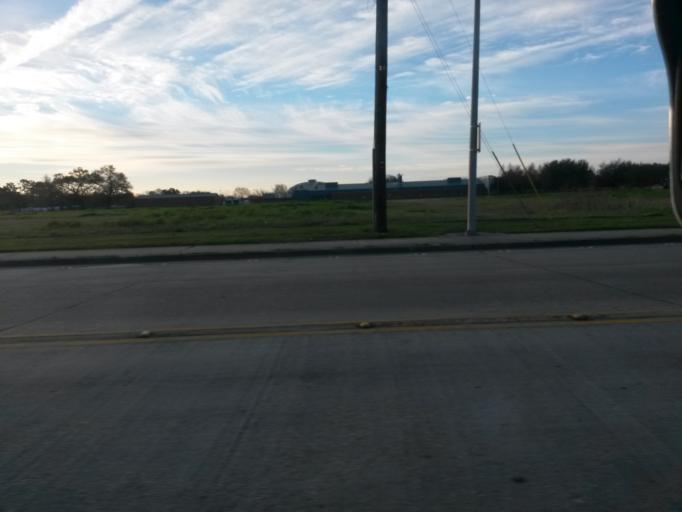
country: US
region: Louisiana
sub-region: Lafayette Parish
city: Lafayette
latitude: 30.2282
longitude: -92.0462
